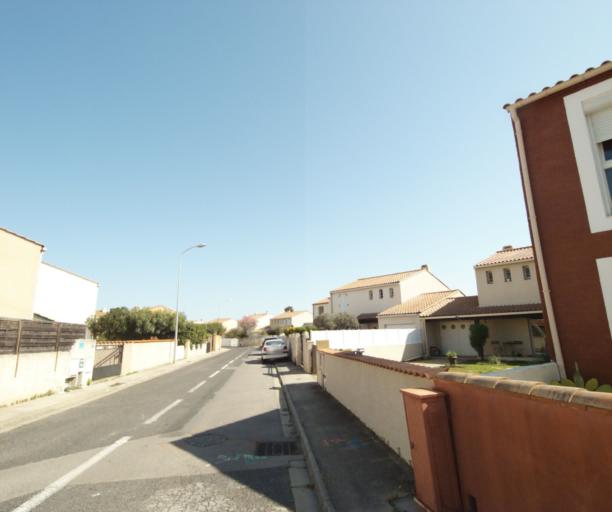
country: FR
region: Languedoc-Roussillon
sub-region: Departement de l'Herault
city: Lattes
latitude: 43.5744
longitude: 3.9127
